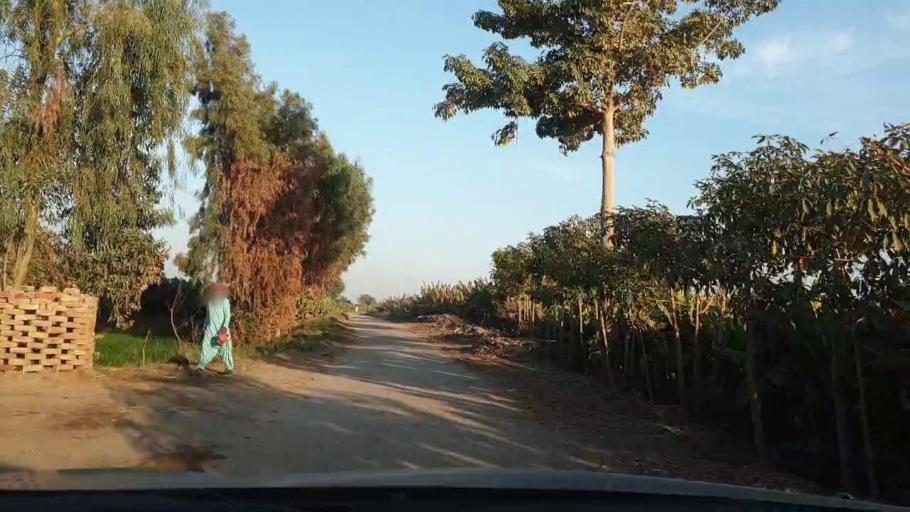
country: PK
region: Sindh
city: Tando Adam
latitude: 25.6168
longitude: 68.6758
